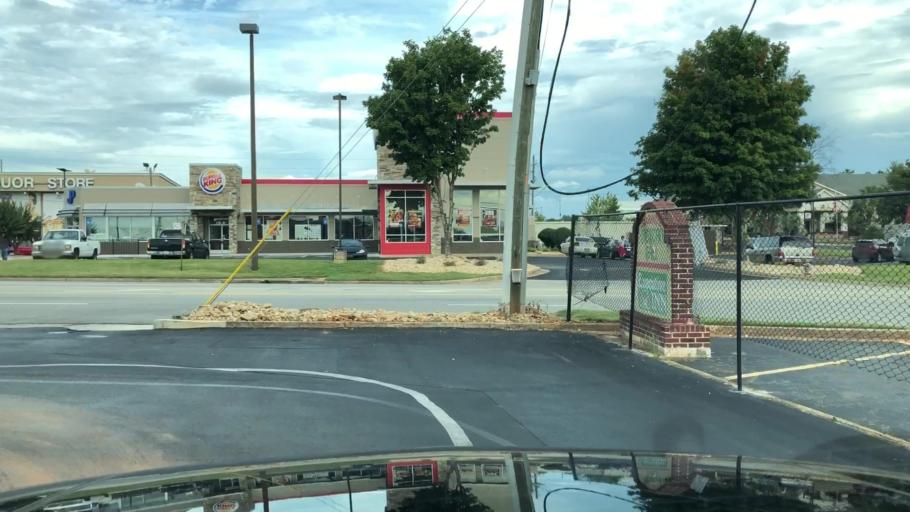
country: US
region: Georgia
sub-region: Henry County
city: Locust Grove
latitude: 33.3531
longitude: -84.1216
